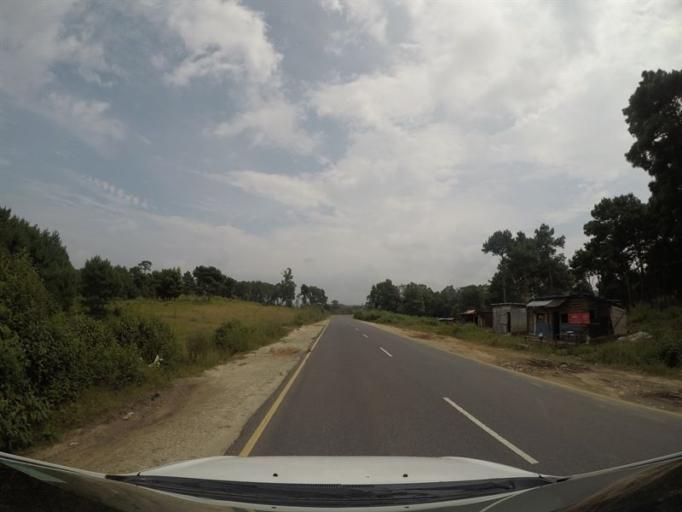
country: IN
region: Meghalaya
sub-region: East Khasi Hills
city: Shillong
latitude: 25.4890
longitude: 92.1905
